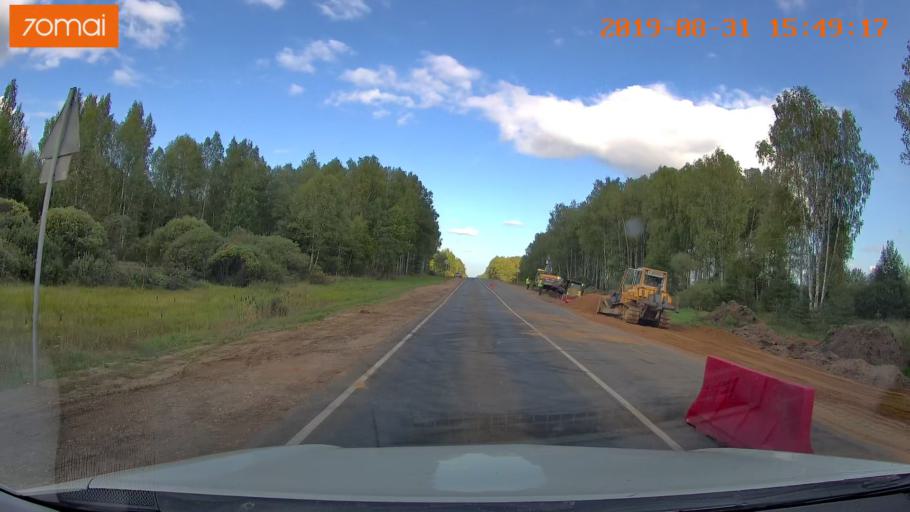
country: RU
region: Kaluga
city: Yukhnov
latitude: 54.6903
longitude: 35.0477
